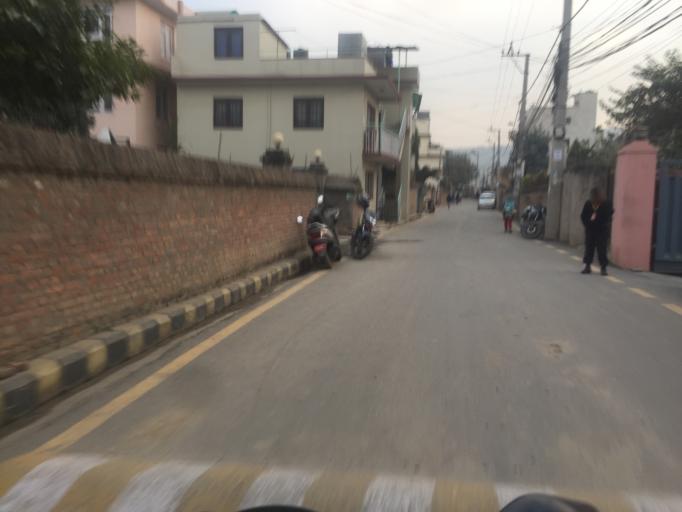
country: NP
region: Central Region
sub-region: Bagmati Zone
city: Patan
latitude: 27.6722
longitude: 85.3085
